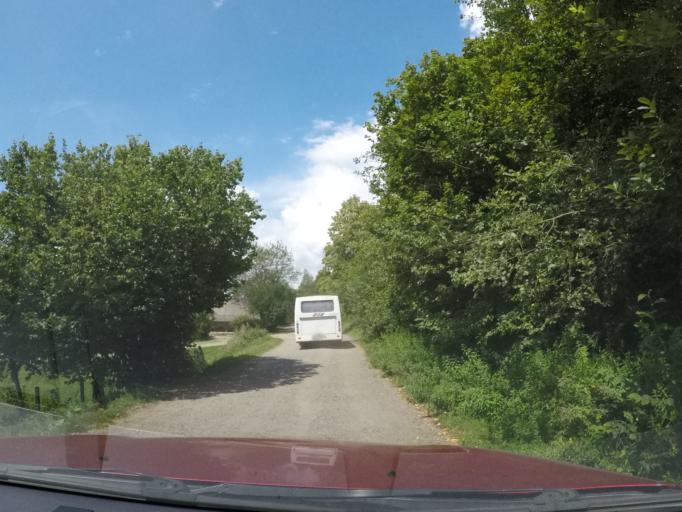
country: UA
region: Zakarpattia
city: Velykyi Bereznyi
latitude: 49.0262
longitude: 22.6032
